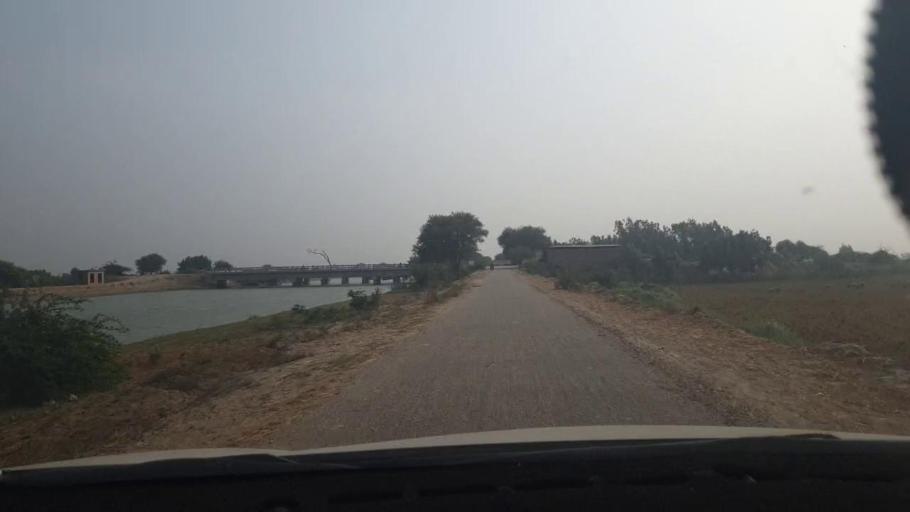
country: PK
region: Sindh
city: Tando Muhammad Khan
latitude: 24.9602
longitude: 68.4962
